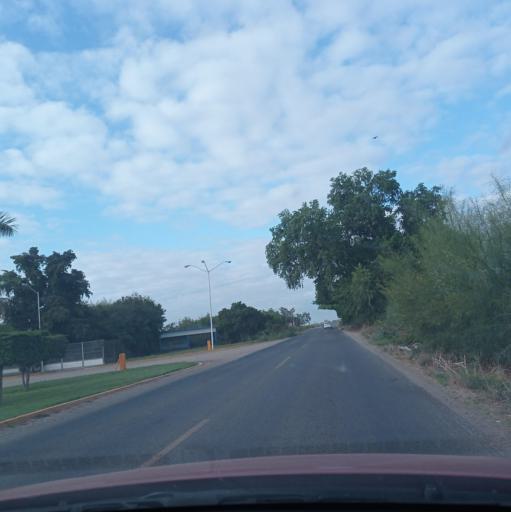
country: MX
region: Sinaloa
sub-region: Guasave
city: Las Quemazones
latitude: 25.6671
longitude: -108.5174
